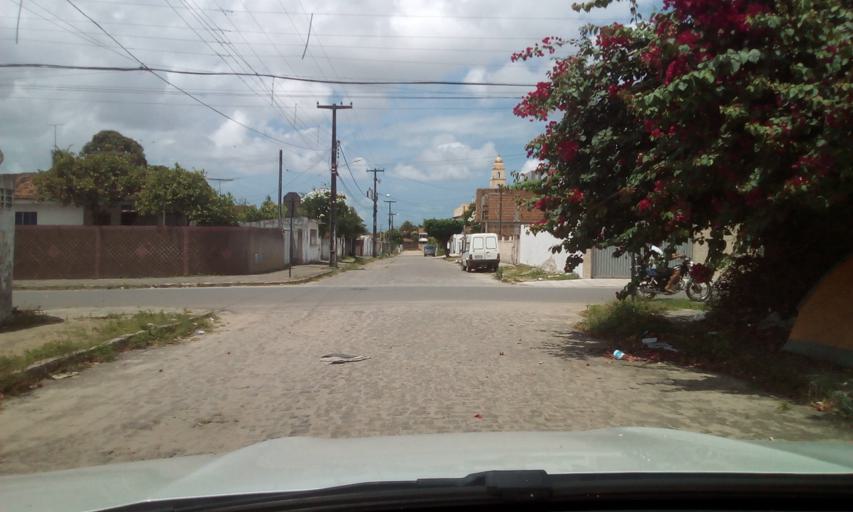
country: BR
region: Paraiba
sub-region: Bayeux
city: Bayeux
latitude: -7.1770
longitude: -34.9158
